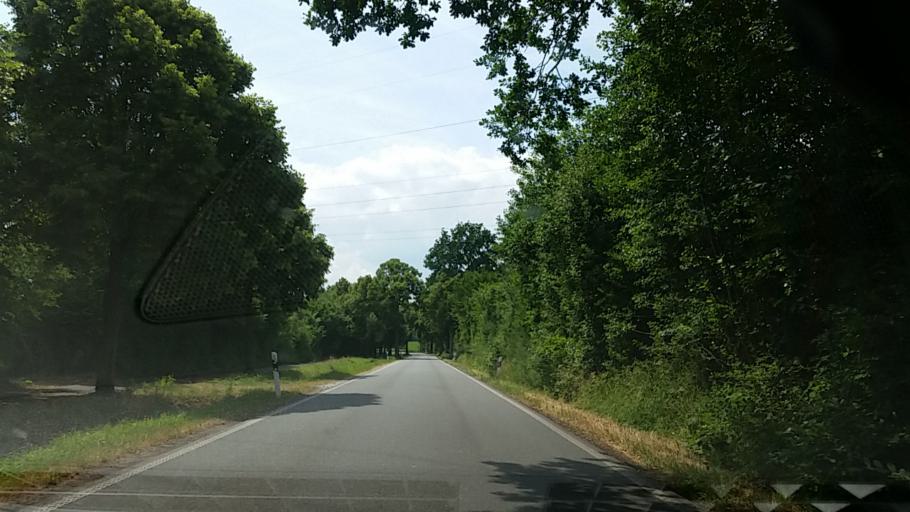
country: DE
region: Schleswig-Holstein
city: Tremsbuttel
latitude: 53.7373
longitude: 10.2971
